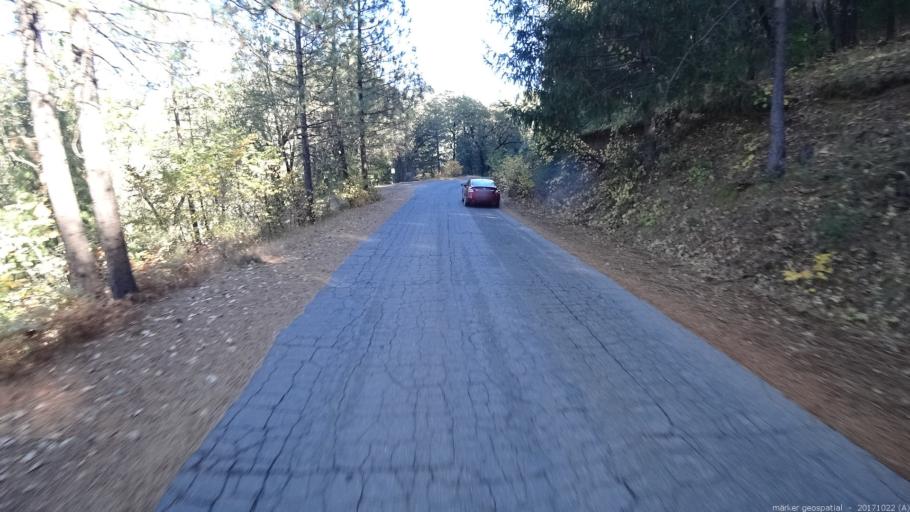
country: US
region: California
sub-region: Shasta County
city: Shasta Lake
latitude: 40.8706
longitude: -122.3634
